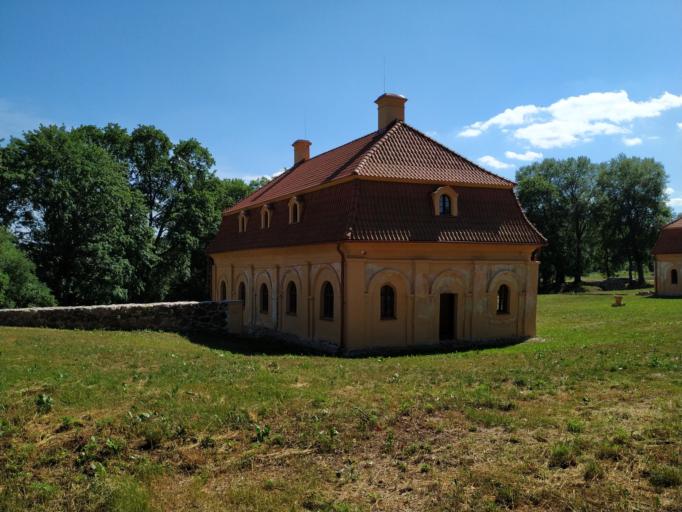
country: LT
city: Nemencine
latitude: 54.8522
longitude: 25.3405
